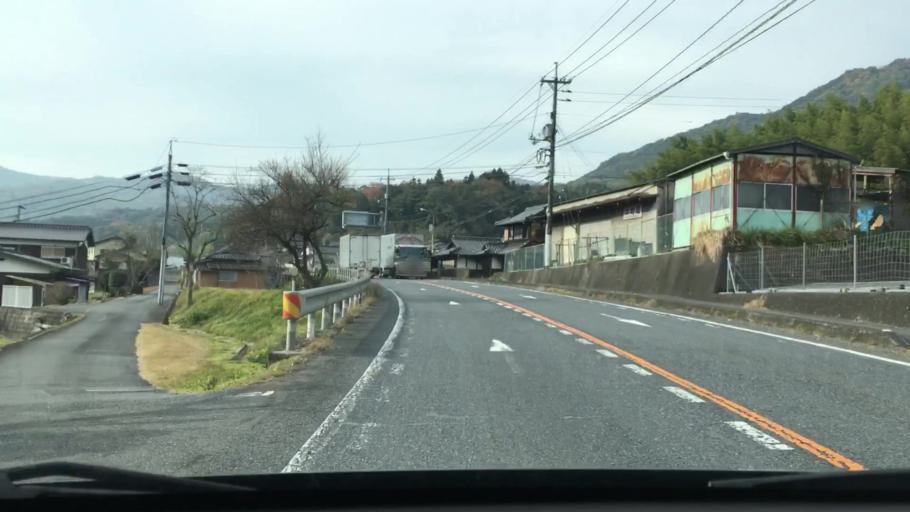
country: JP
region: Yamaguchi
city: Yanai
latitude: 34.0930
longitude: 132.0250
